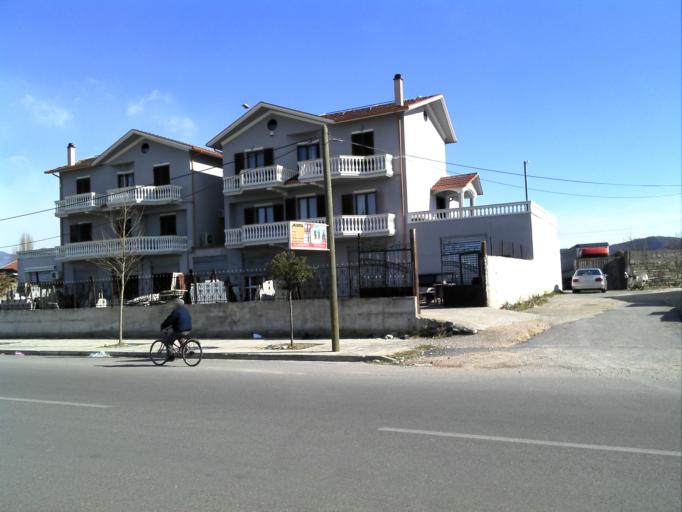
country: AL
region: Shkoder
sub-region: Rrethi i Shkodres
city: Shkoder
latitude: 42.0828
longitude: 19.5300
